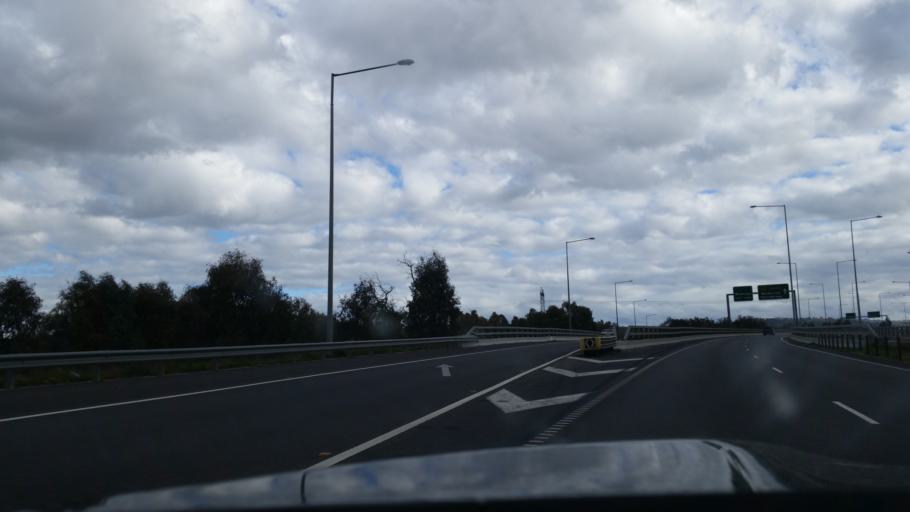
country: AU
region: Victoria
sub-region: Wodonga
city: Wodonga
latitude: -36.1082
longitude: 146.9025
